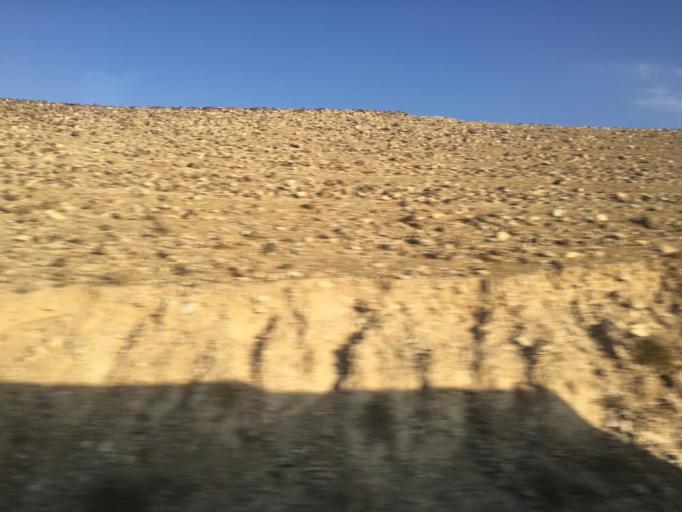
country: IL
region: Southern District
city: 'Arad
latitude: 31.3041
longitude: 35.2534
